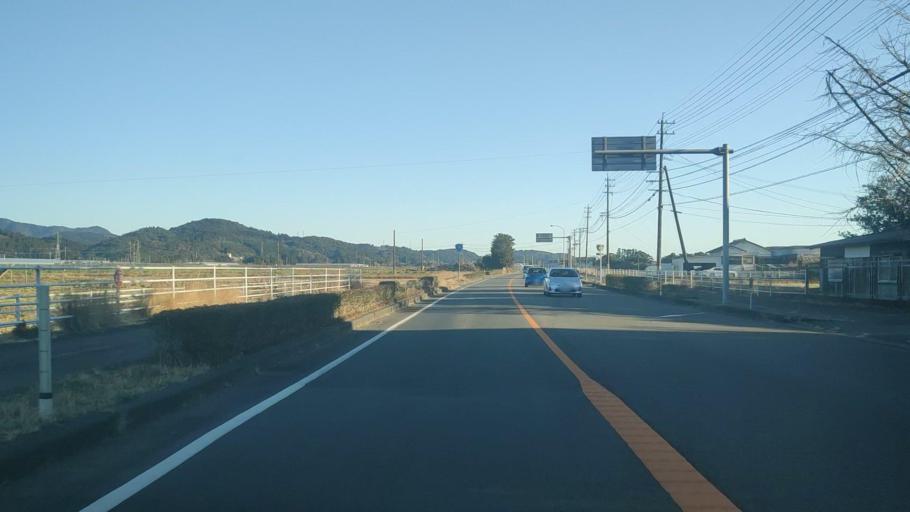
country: JP
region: Miyazaki
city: Takanabe
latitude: 32.3175
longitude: 131.5918
